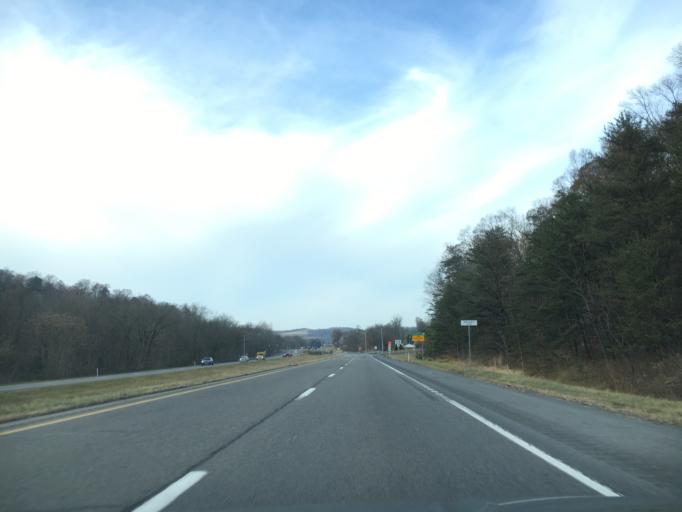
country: US
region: Pennsylvania
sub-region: Montour County
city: Danville
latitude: 40.9805
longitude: -76.6258
